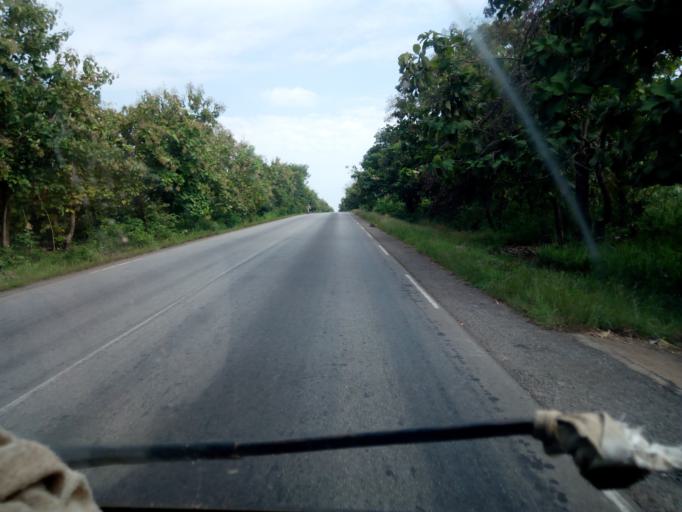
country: TG
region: Plateaux
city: Notse
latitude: 7.0048
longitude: 1.1649
